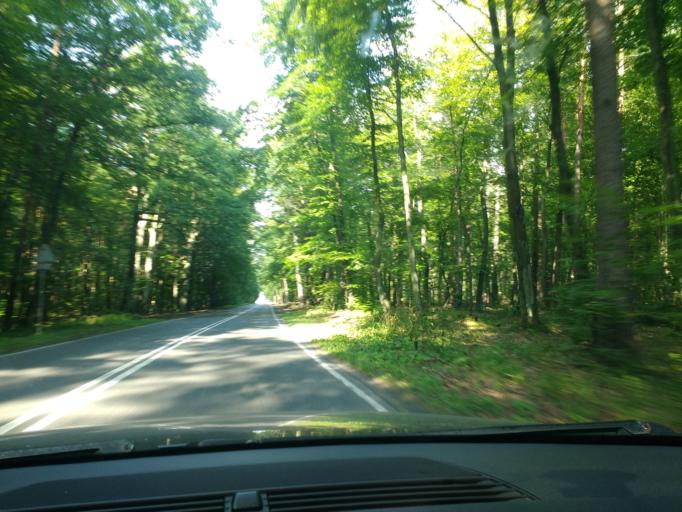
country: PL
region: Pomeranian Voivodeship
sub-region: Gdynia
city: Wielki Kack
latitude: 54.4609
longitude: 18.5086
